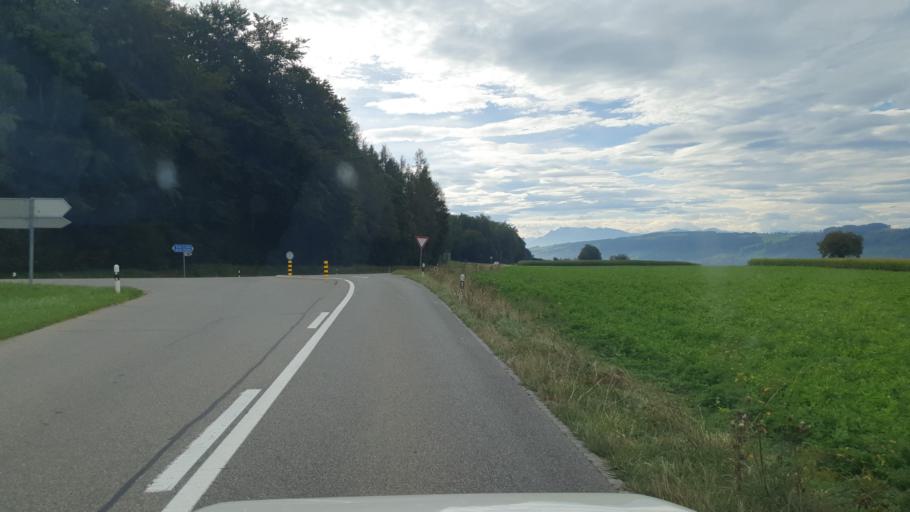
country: CH
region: Aargau
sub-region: Bezirk Lenzburg
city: Meisterschwanden
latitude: 47.2850
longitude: 8.2337
